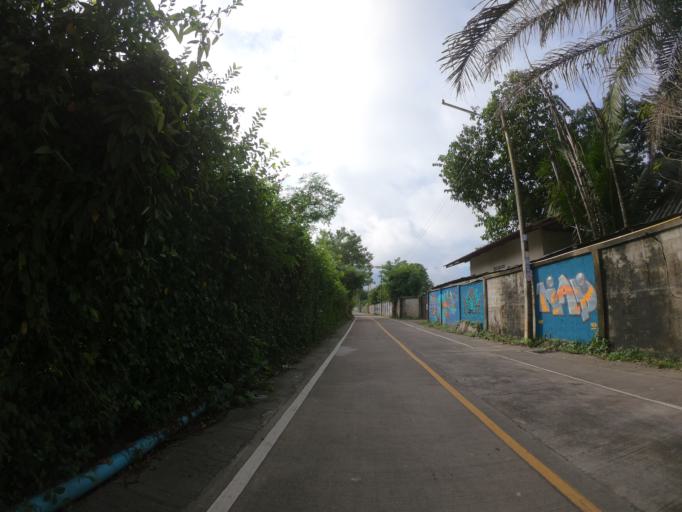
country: TH
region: Chiang Mai
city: Chiang Mai
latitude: 18.8182
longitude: 98.9645
